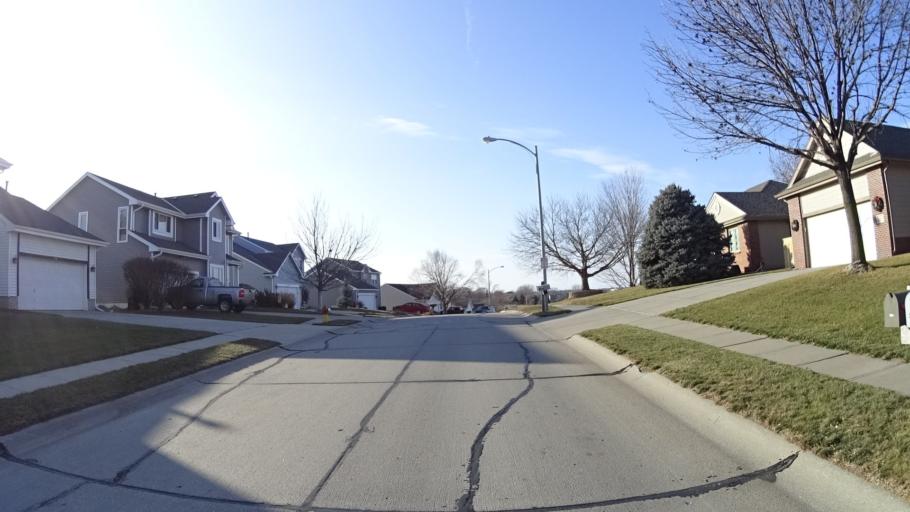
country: US
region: Nebraska
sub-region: Sarpy County
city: Offutt Air Force Base
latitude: 41.1354
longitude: -95.9517
